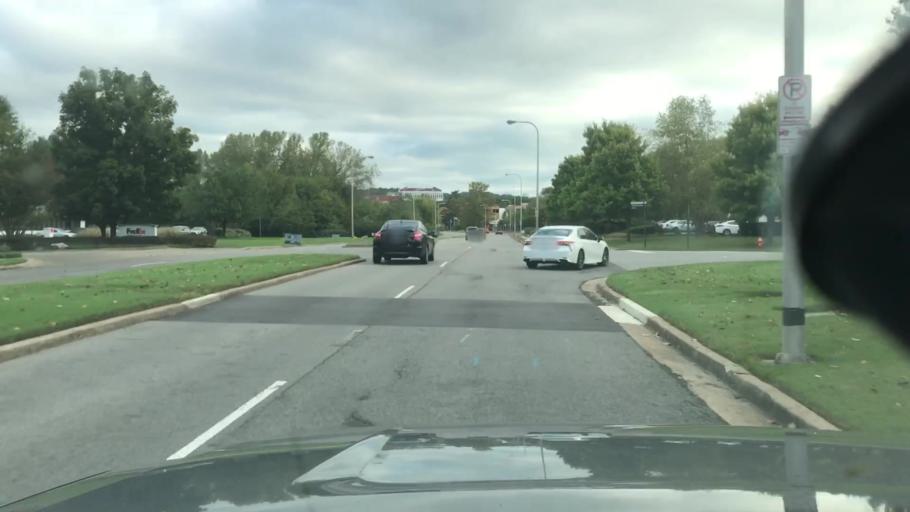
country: US
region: Tennessee
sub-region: Davidson County
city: Nashville
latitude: 36.1960
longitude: -86.7995
